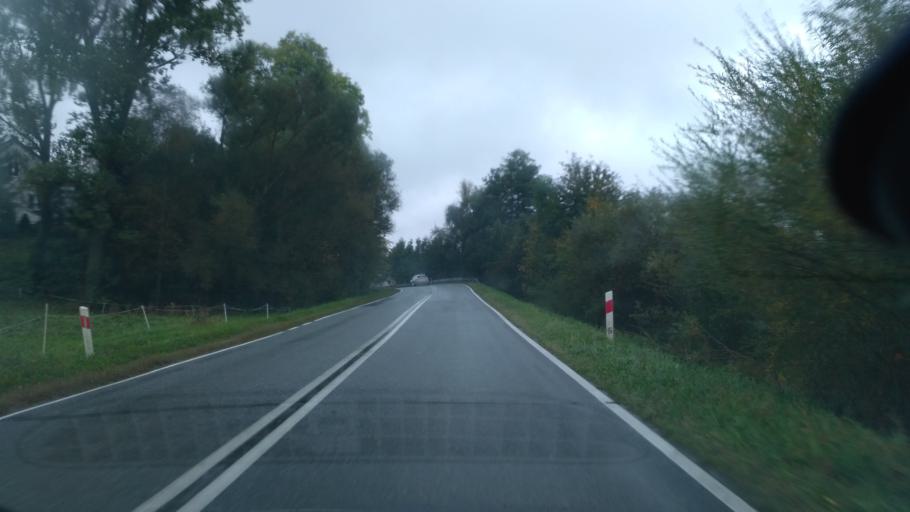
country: PL
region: Subcarpathian Voivodeship
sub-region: Powiat ropczycko-sedziszowski
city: Niedzwiada
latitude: 49.9794
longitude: 21.5595
